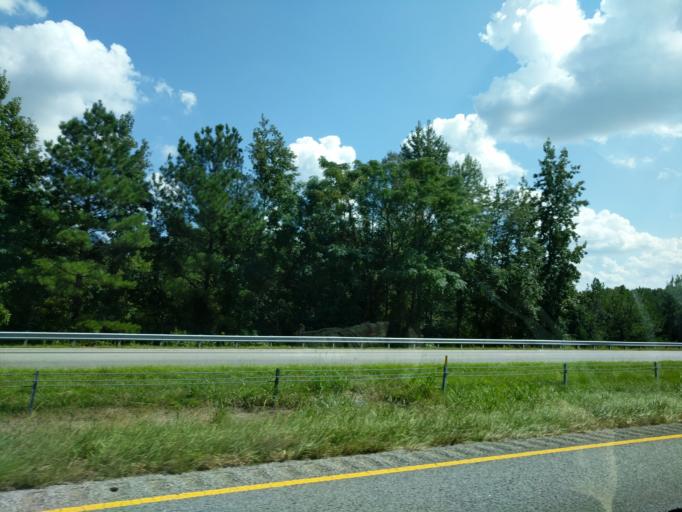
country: US
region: South Carolina
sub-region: Spartanburg County
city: Roebuck
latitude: 34.8923
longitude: -81.9931
